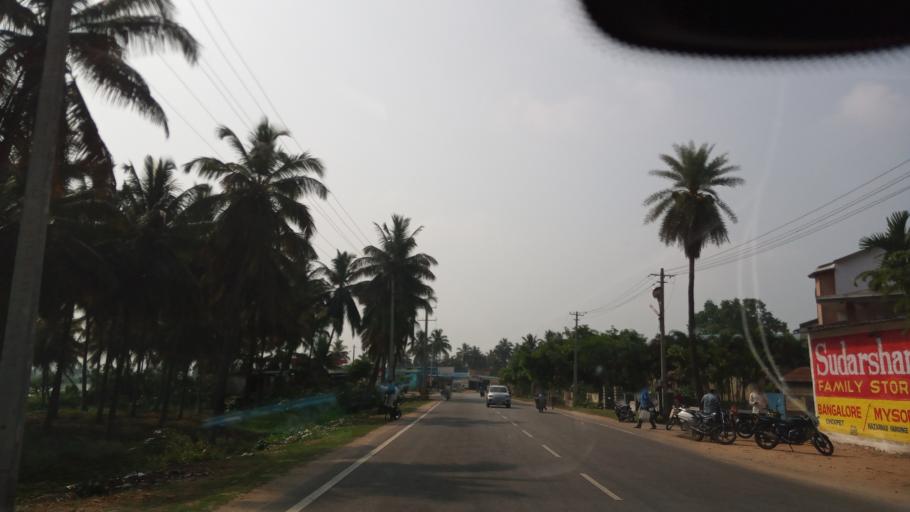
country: IN
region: Karnataka
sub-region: Mandya
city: Pandavapura
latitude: 12.5043
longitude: 76.6760
